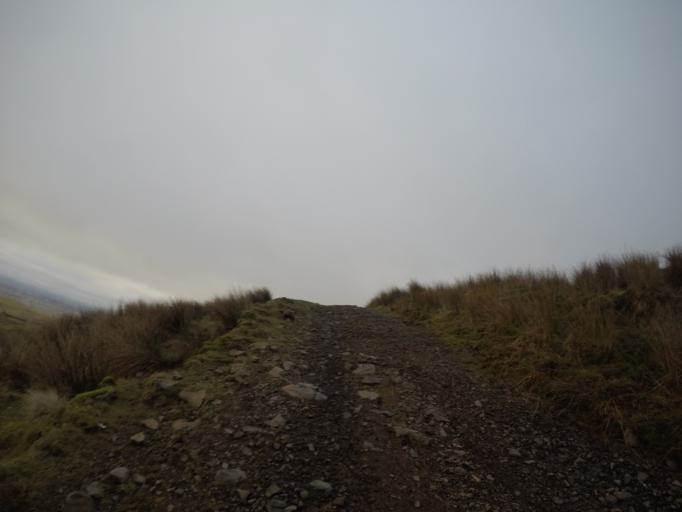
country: GB
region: Scotland
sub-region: North Ayrshire
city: Dalry
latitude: 55.7346
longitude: -4.7683
